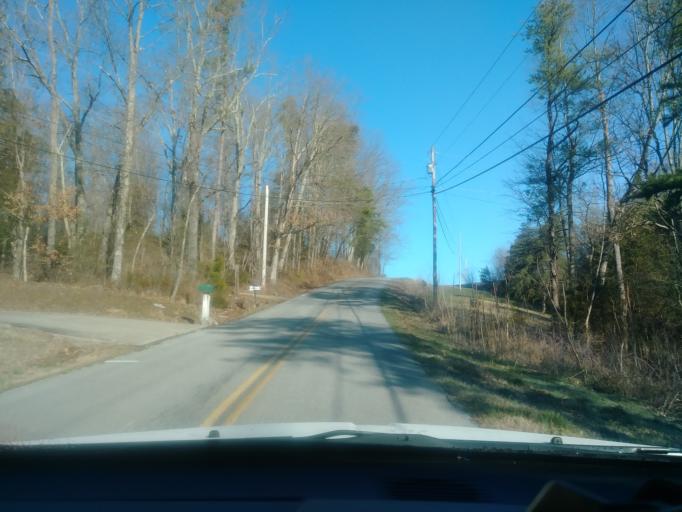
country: US
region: Tennessee
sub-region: Greene County
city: Mosheim
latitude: 36.1052
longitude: -82.9286
